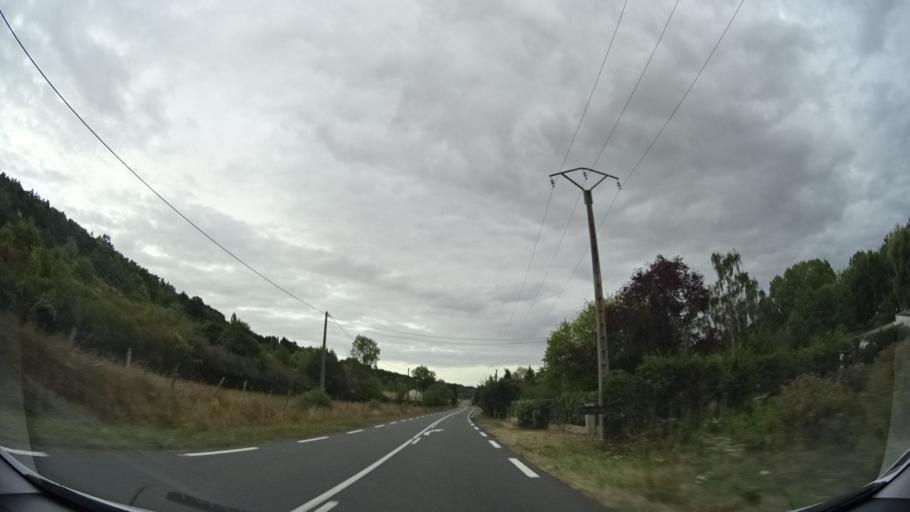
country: FR
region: Centre
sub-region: Departement du Loiret
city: Trigueres
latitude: 47.9448
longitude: 3.0121
